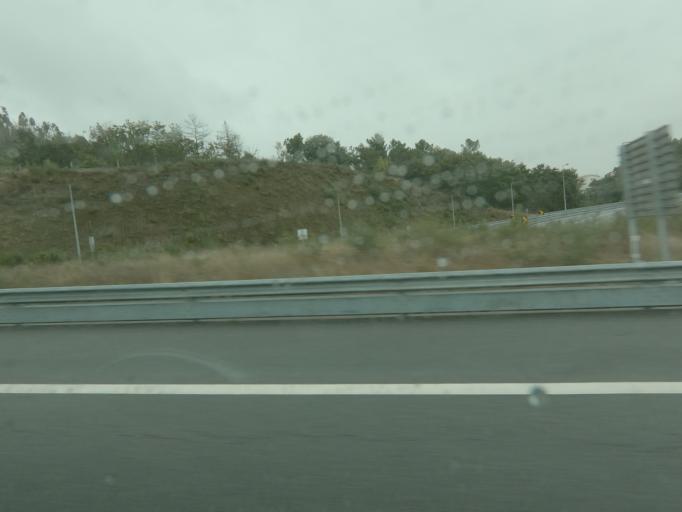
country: PT
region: Porto
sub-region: Amarante
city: Amarante
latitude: 41.2622
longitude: -8.0721
